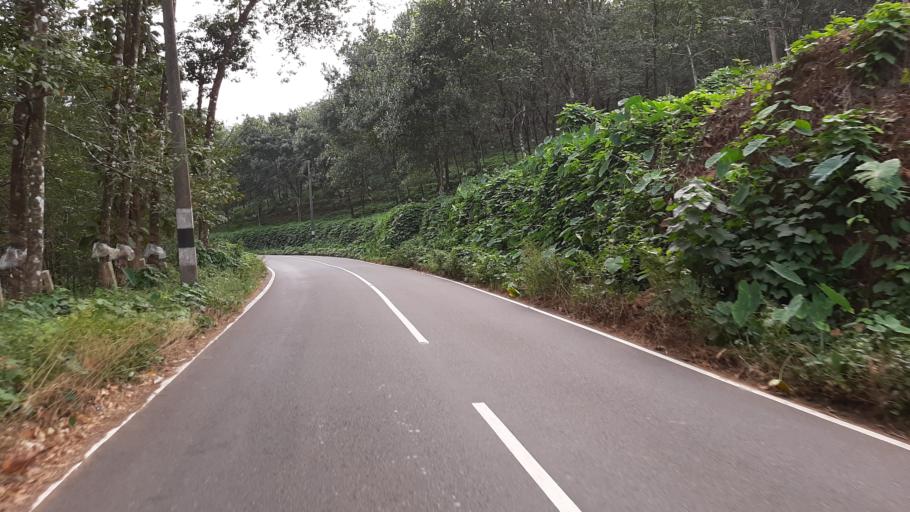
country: IN
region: Kerala
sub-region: Pattanamtitta
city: Pathanamthitta
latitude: 9.4636
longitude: 76.8698
